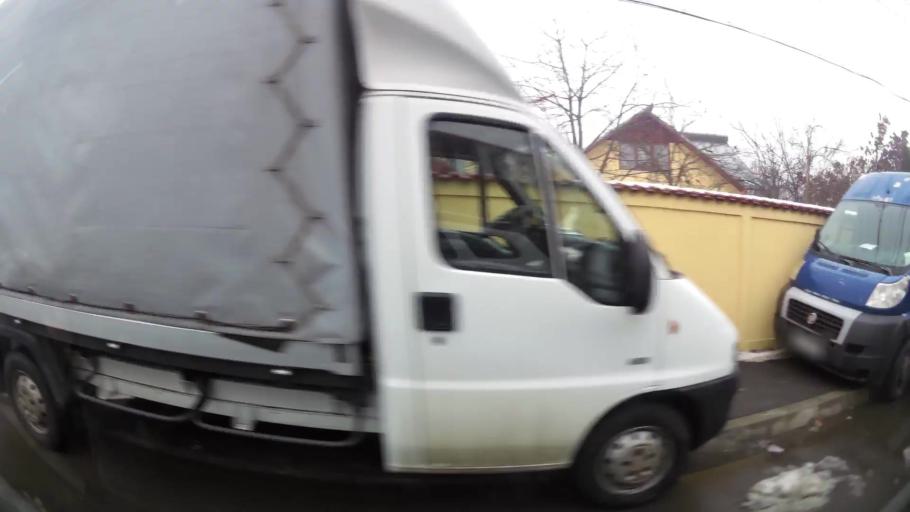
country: RO
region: Ilfov
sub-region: Comuna Chiajna
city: Rosu
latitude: 44.4714
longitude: 26.0083
